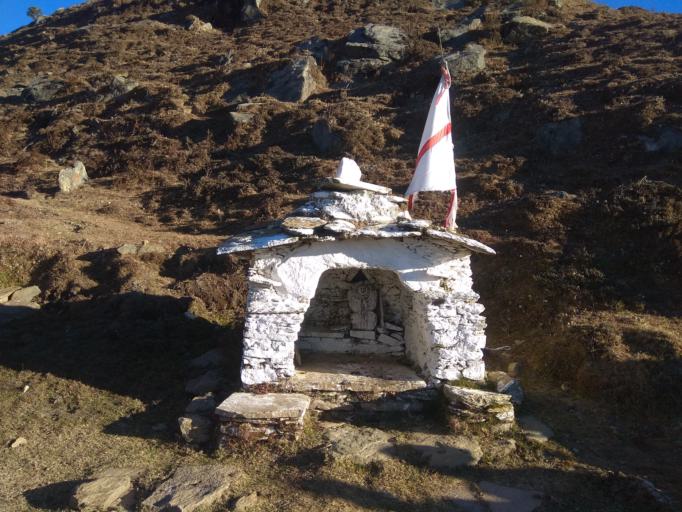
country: NP
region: Far Western
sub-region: Seti Zone
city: Achham
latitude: 29.2777
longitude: 81.6502
